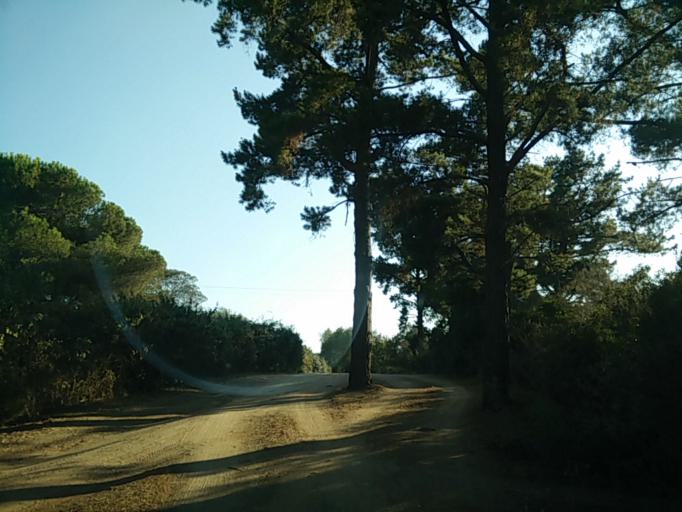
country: FR
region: Corsica
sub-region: Departement de la Corse-du-Sud
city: Pietrosella
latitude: 41.8453
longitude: 8.7662
